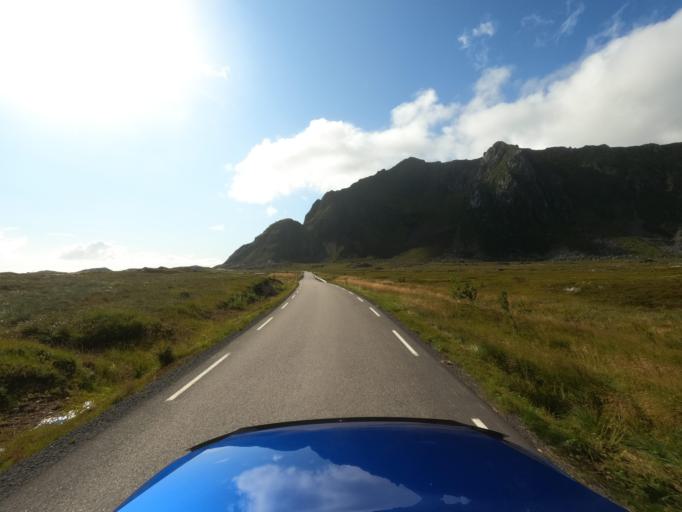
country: NO
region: Nordland
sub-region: Vestvagoy
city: Evjen
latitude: 68.2055
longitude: 14.0400
